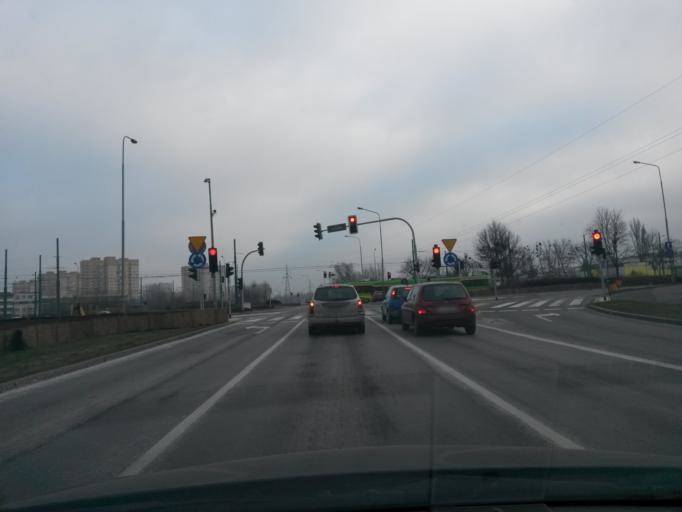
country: PL
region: Greater Poland Voivodeship
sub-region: Poznan
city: Poznan
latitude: 52.3802
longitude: 16.9419
